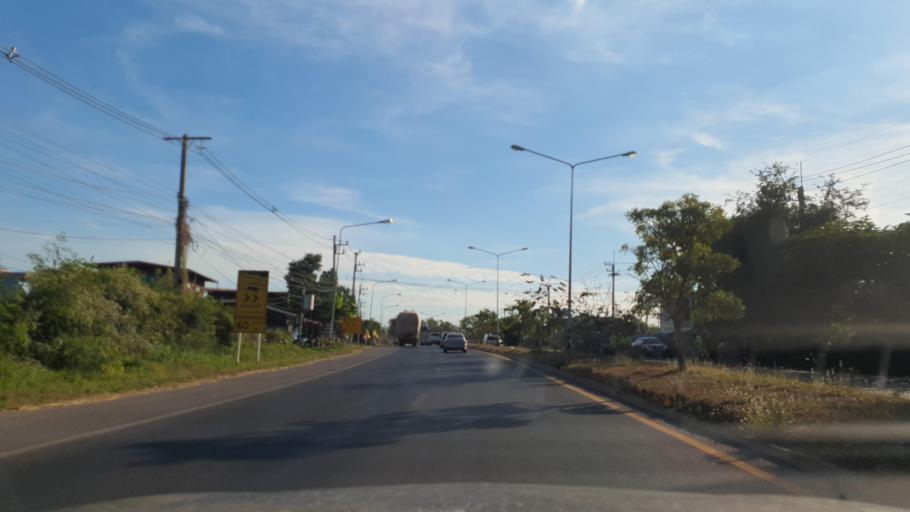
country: TH
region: Kalasin
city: Yang Talat
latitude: 16.3727
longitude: 103.3453
